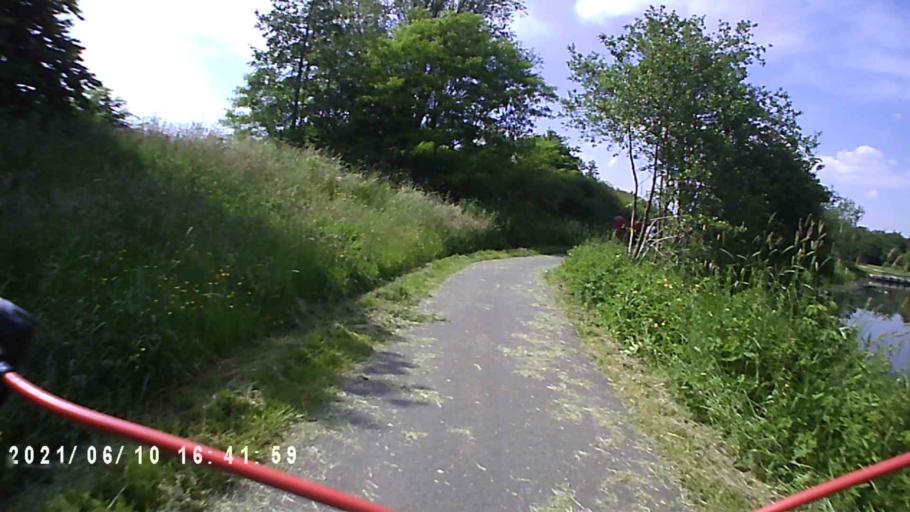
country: NL
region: Friesland
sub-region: Gemeente Achtkarspelen
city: Buitenpost
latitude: 53.2454
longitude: 6.1362
